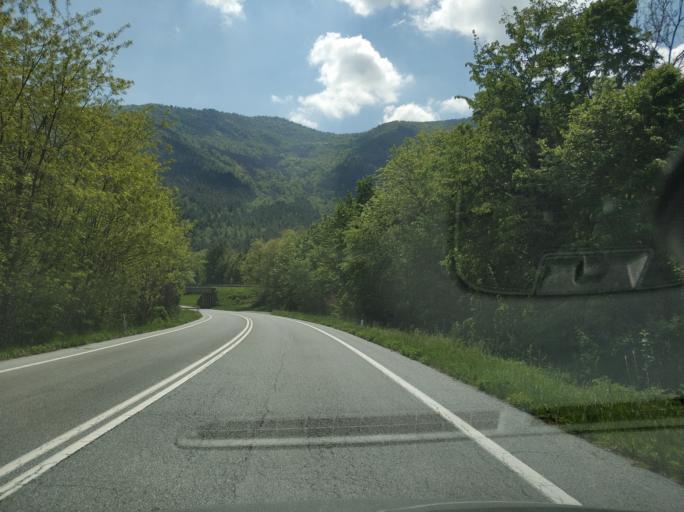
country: IT
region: Piedmont
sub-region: Provincia di Torino
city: Germagnano
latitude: 45.2586
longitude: 7.4619
